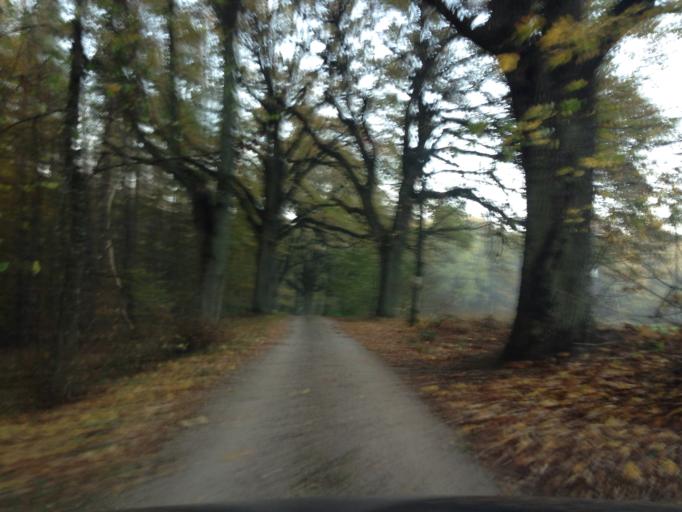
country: PL
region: Warmian-Masurian Voivodeship
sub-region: Powiat dzialdowski
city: Lidzbark
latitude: 53.2497
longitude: 19.7641
